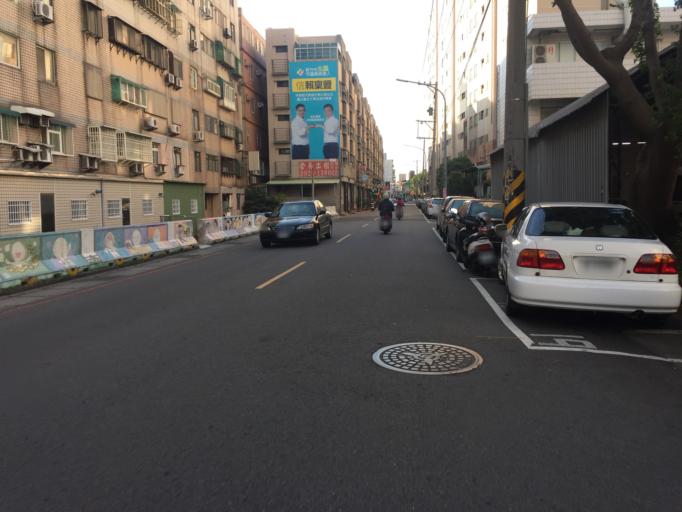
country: TW
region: Taiwan
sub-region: Hsinchu
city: Hsinchu
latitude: 24.8162
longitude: 120.9794
